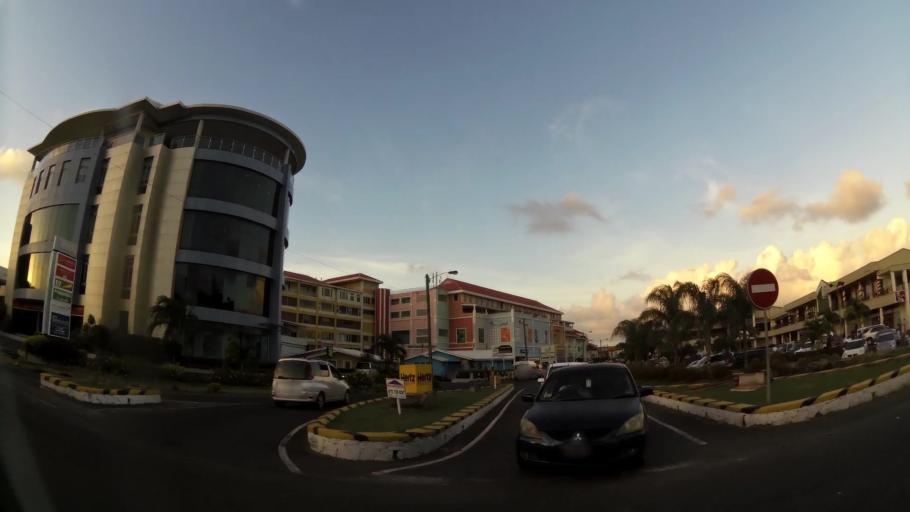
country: LC
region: Gros-Islet
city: Gros Islet
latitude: 14.0679
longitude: -60.9543
